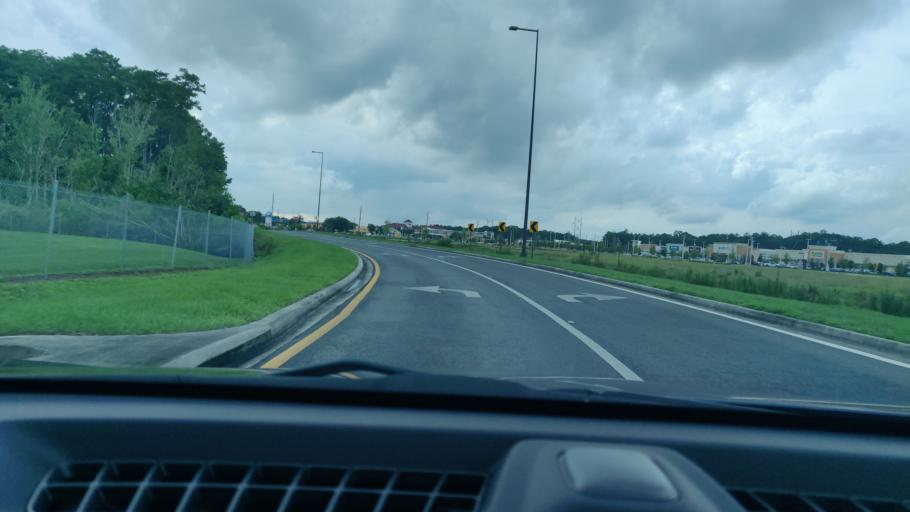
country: US
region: Florida
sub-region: Osceola County
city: Celebration
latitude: 28.3432
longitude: -81.4810
